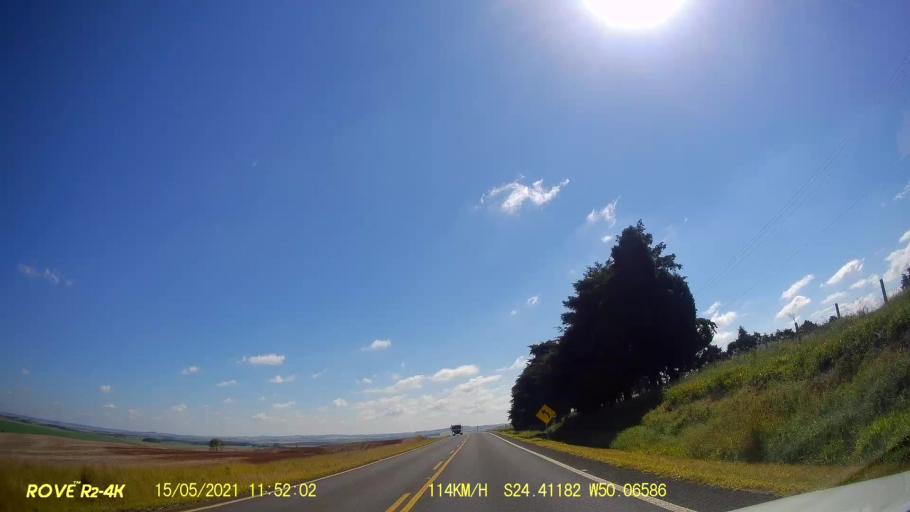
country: BR
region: Parana
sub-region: Pirai Do Sul
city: Pirai do Sul
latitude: -24.4096
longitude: -50.0672
